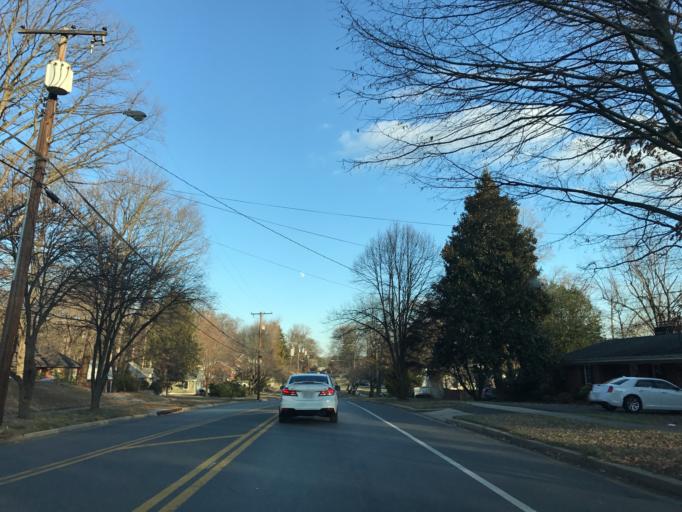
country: US
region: Maryland
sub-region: Montgomery County
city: Wheaton
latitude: 39.0471
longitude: -77.0476
